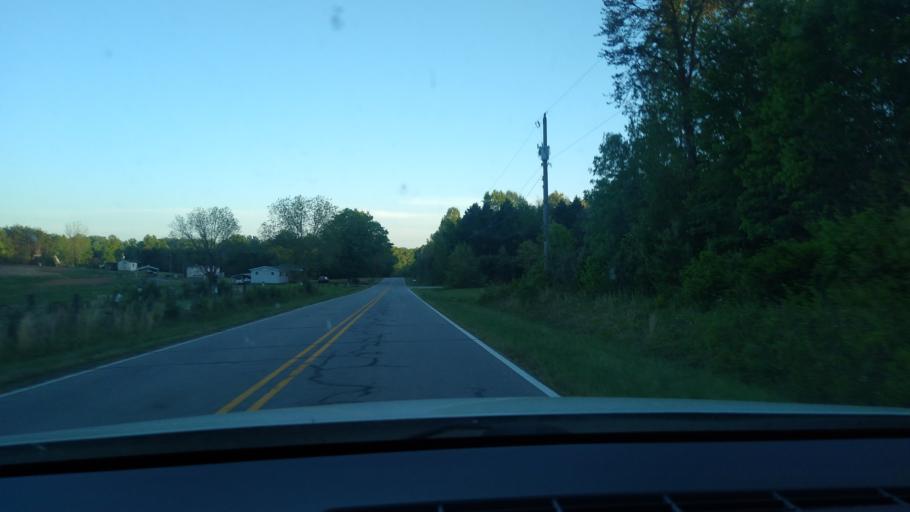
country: US
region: North Carolina
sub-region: Rockingham County
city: Reidsville
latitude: 36.3825
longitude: -79.5541
